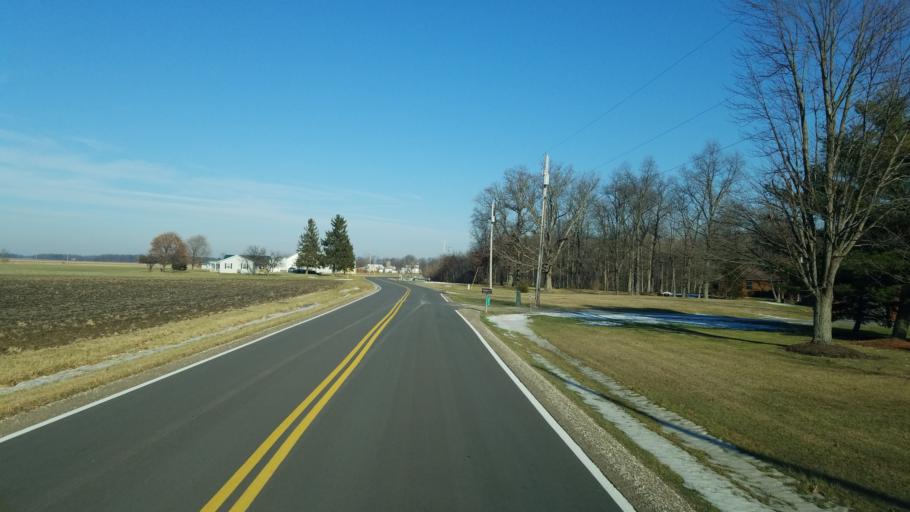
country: US
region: Ohio
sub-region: Huron County
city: Monroeville
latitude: 41.2785
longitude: -82.6825
